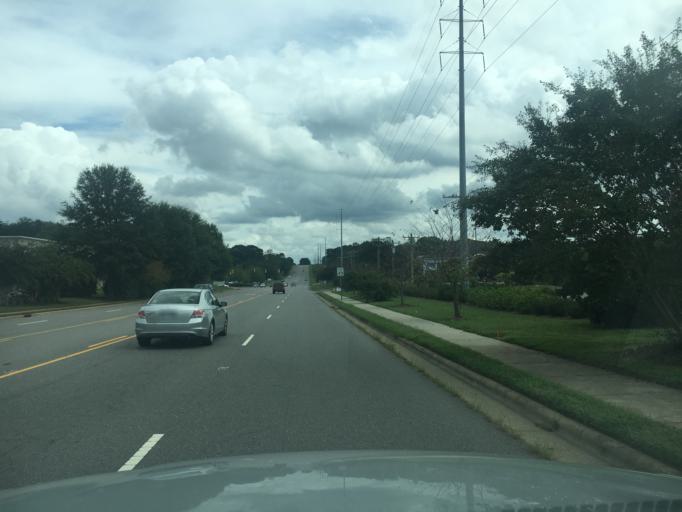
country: US
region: North Carolina
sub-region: Catawba County
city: Hickory
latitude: 35.7010
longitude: -81.3043
